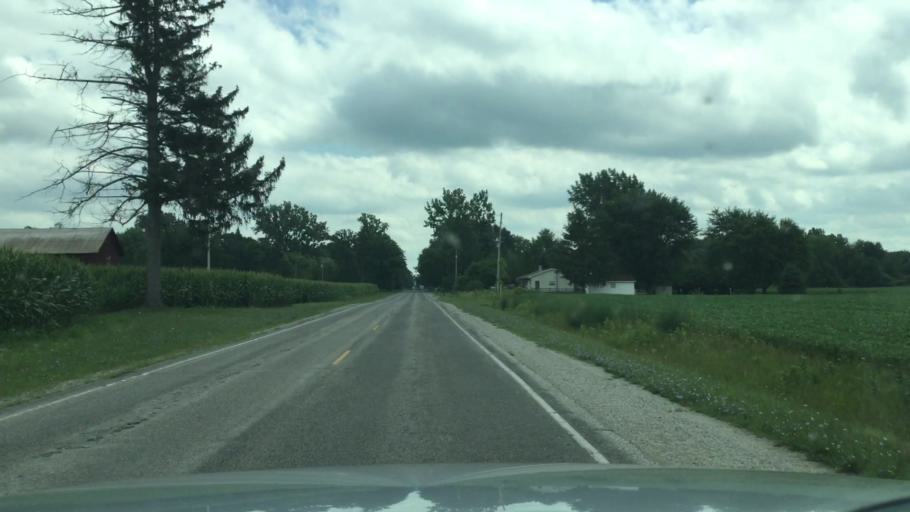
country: US
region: Michigan
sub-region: Saginaw County
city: Birch Run
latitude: 43.2934
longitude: -83.8134
